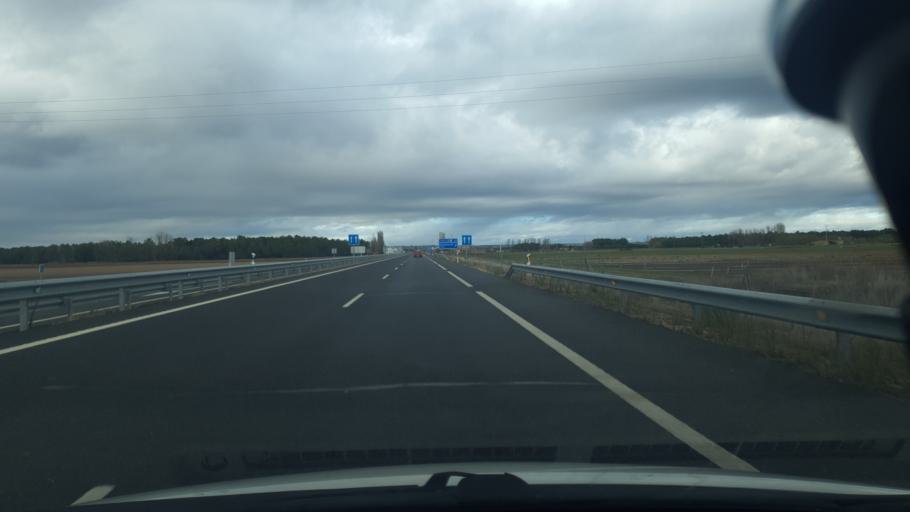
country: ES
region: Castille and Leon
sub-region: Provincia de Segovia
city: Sanchonuno
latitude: 41.3016
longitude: -4.3013
